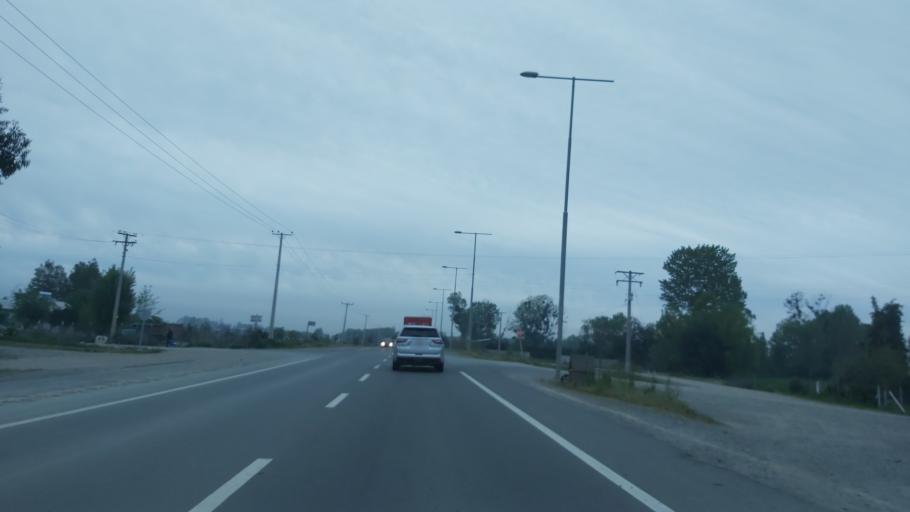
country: CL
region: Maule
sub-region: Provincia de Linares
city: Linares
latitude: -35.8298
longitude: -71.6129
